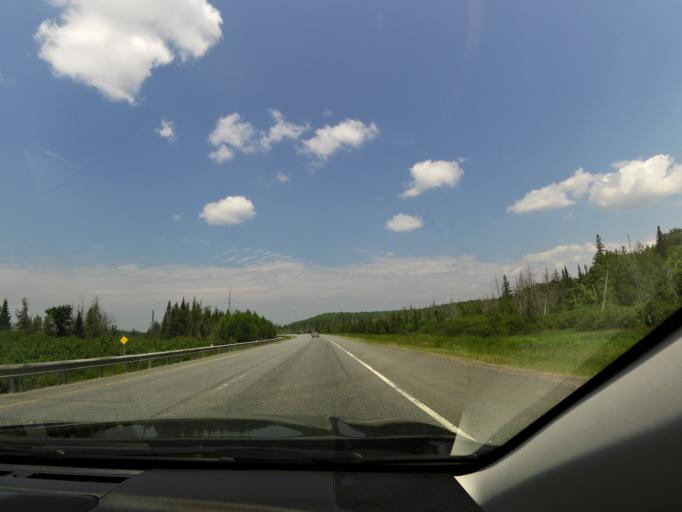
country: CA
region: Ontario
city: Huntsville
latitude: 45.4284
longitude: -79.2385
